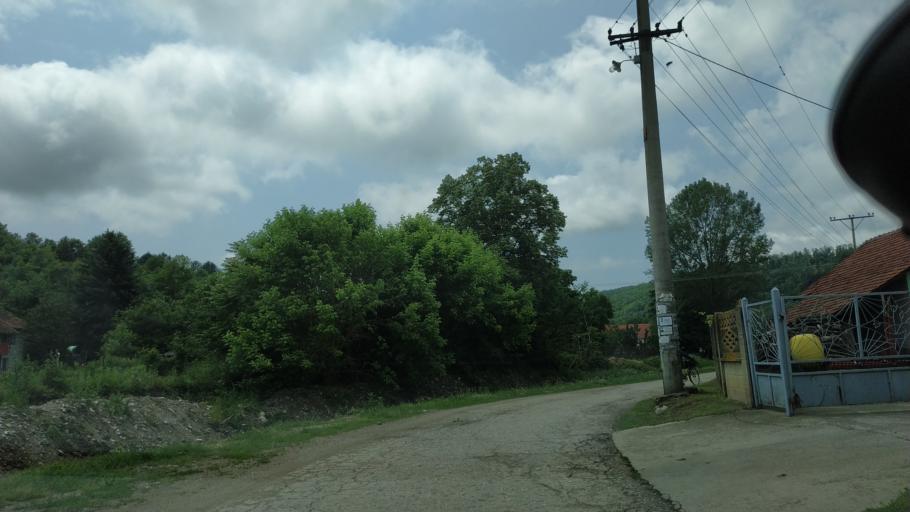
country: RS
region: Central Serbia
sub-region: Nisavski Okrug
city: Aleksinac
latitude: 43.4214
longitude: 21.7046
